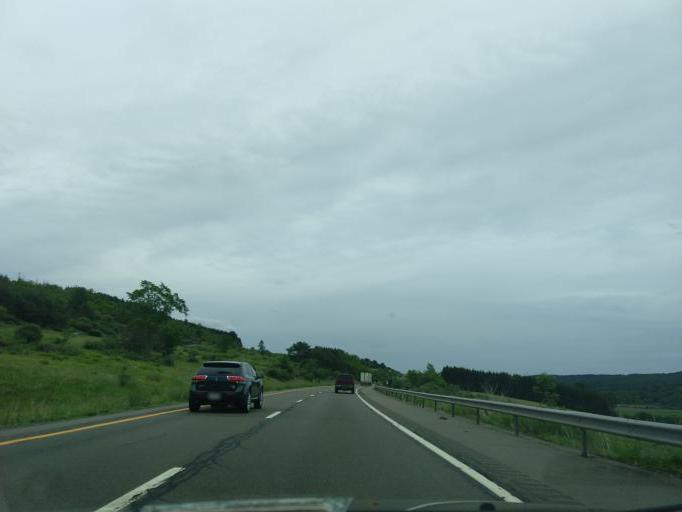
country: US
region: New York
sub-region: Chenango County
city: Lakeview
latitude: 42.4256
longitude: -76.0193
